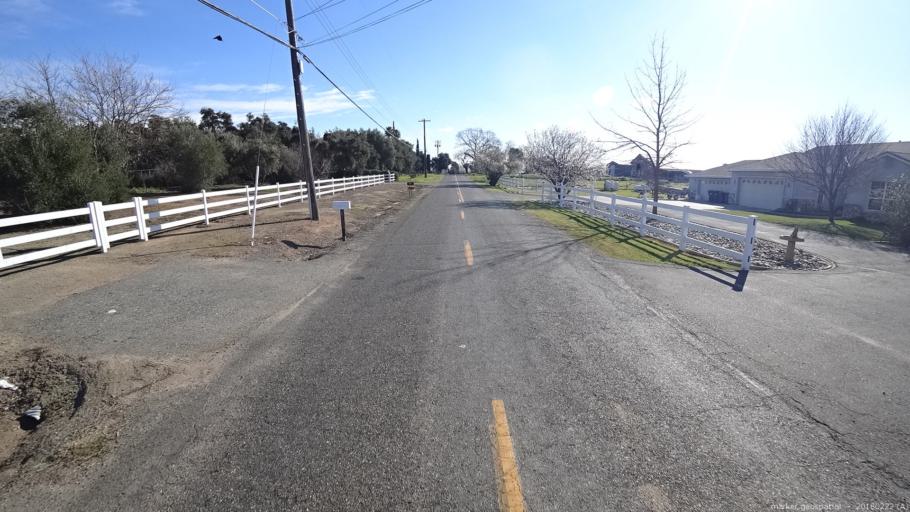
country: US
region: California
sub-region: Sacramento County
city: Elverta
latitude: 38.7295
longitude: -121.4545
